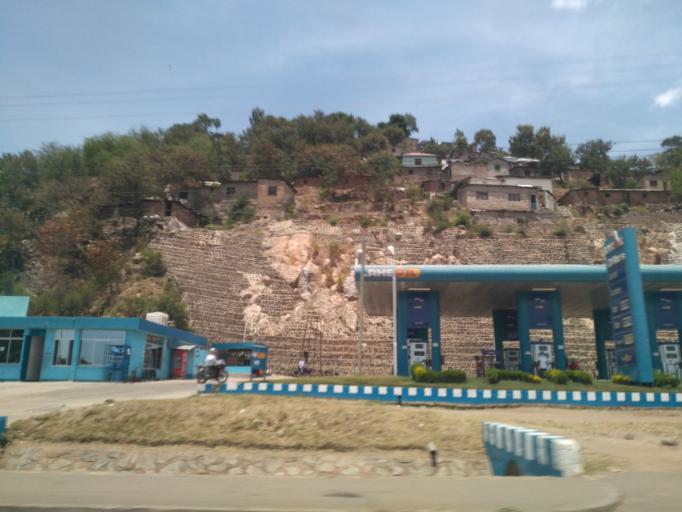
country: TZ
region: Mwanza
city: Mwanza
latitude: -2.5275
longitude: 32.9013
